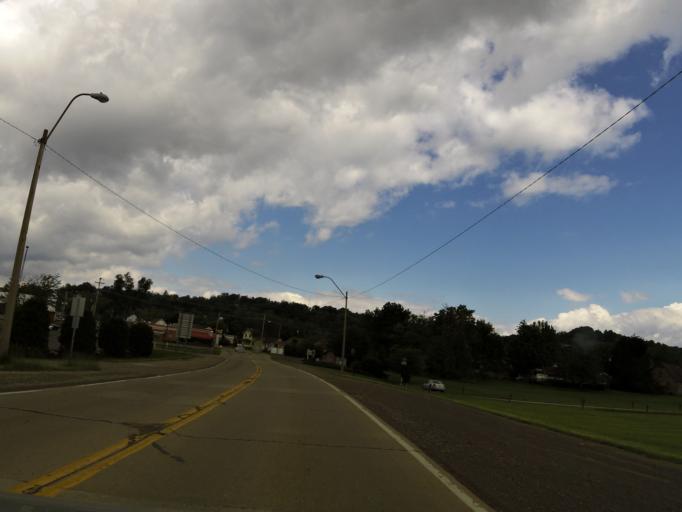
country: US
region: Ohio
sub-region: Athens County
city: Athens
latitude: 39.3313
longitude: -82.0883
